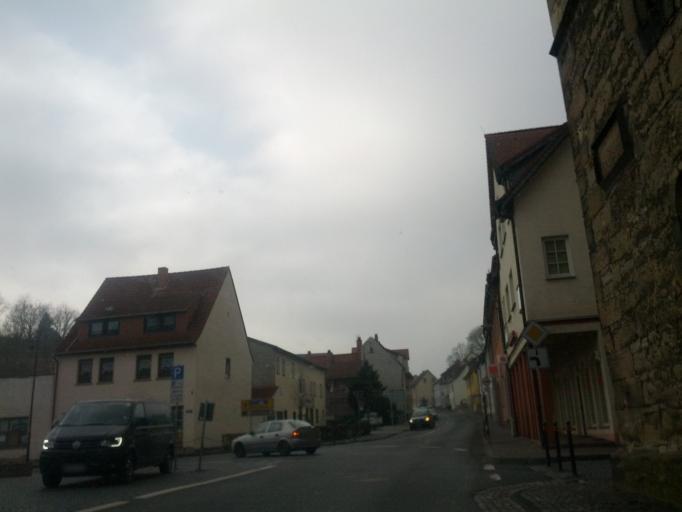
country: DE
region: Thuringia
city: Creuzburg
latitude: 51.0527
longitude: 10.2482
